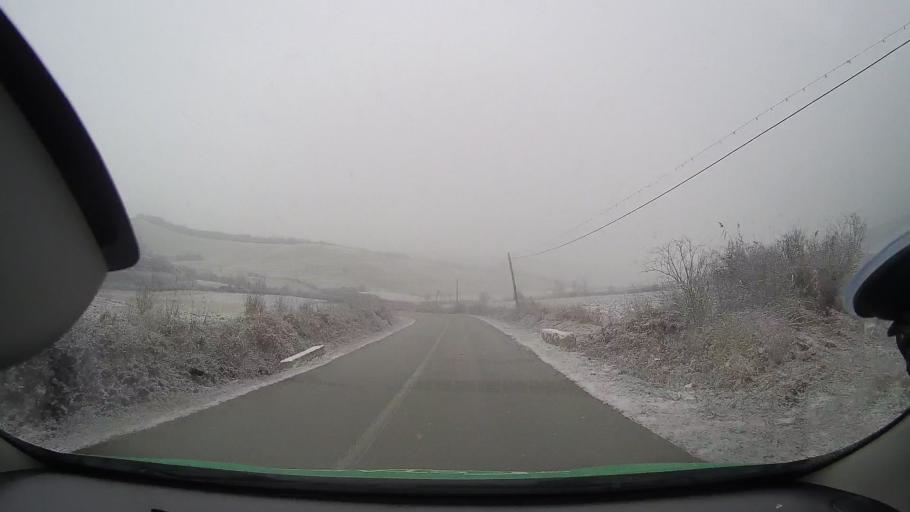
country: RO
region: Alba
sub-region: Comuna Lopadea Noua
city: Lopadea Noua
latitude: 46.2958
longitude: 23.8426
